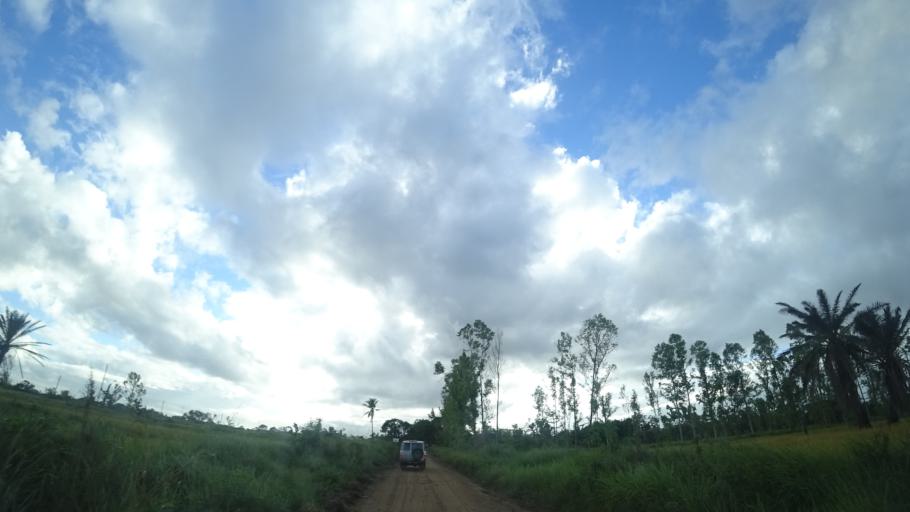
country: MZ
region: Sofala
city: Beira
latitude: -19.7189
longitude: 35.0026
